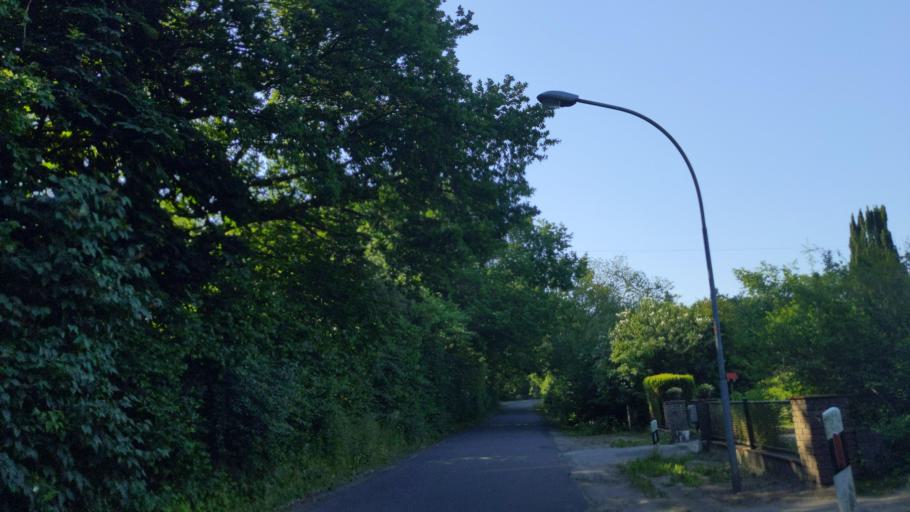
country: DE
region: Schleswig-Holstein
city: Ratekau
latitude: 53.9261
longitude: 10.7682
